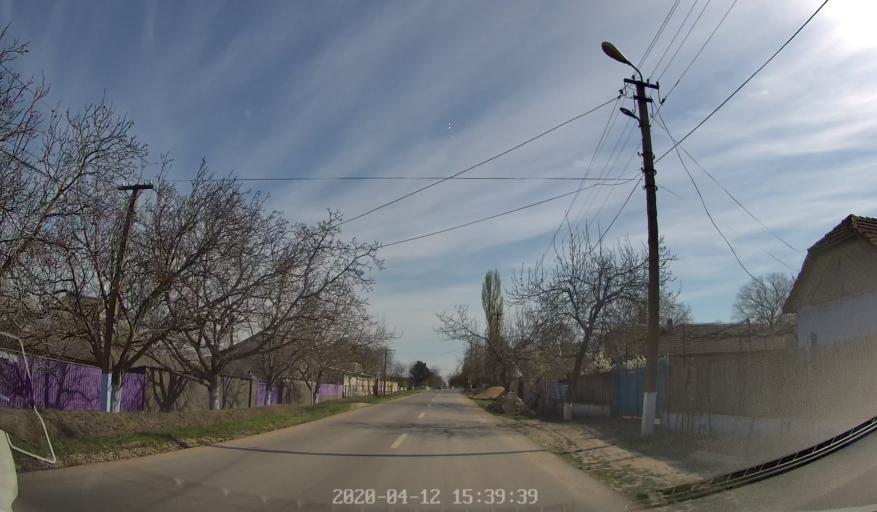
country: MD
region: Telenesti
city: Cocieri
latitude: 47.3142
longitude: 29.0714
